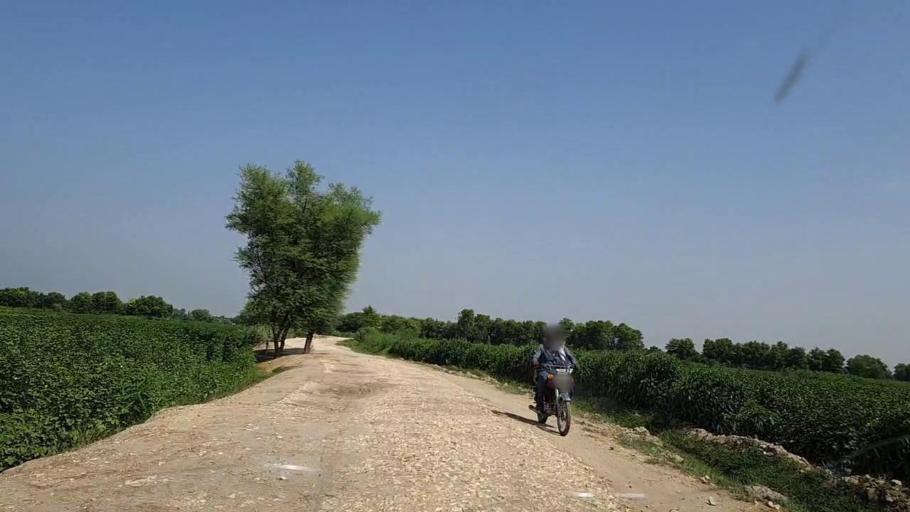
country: PK
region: Sindh
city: Khanpur
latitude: 27.7487
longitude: 69.3471
